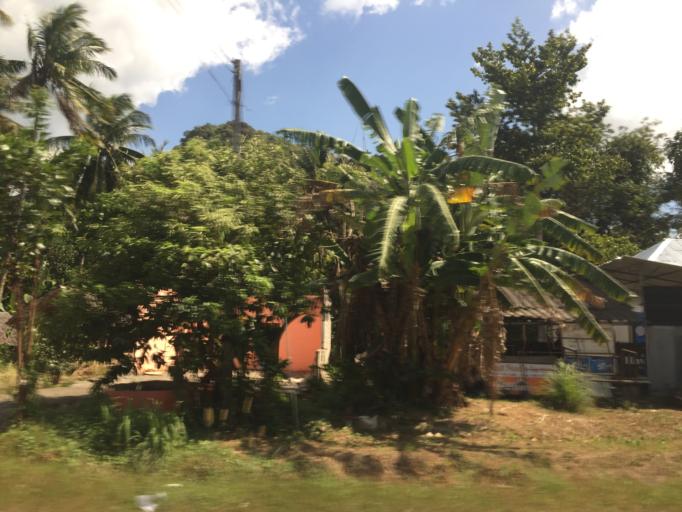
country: TH
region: Phangnga
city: Ban Ao Nang
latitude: 8.0507
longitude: 98.8381
